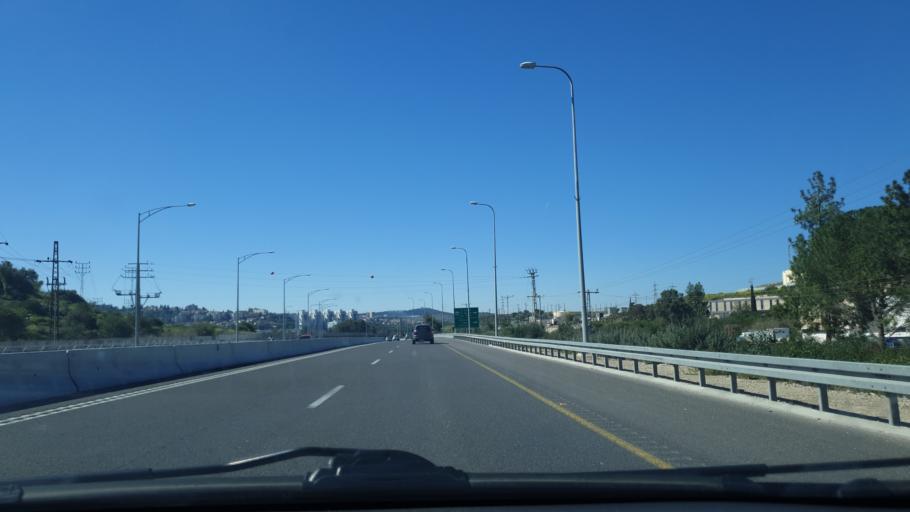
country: IL
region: Jerusalem
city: Bet Shemesh
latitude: 31.7708
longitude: 35.0005
